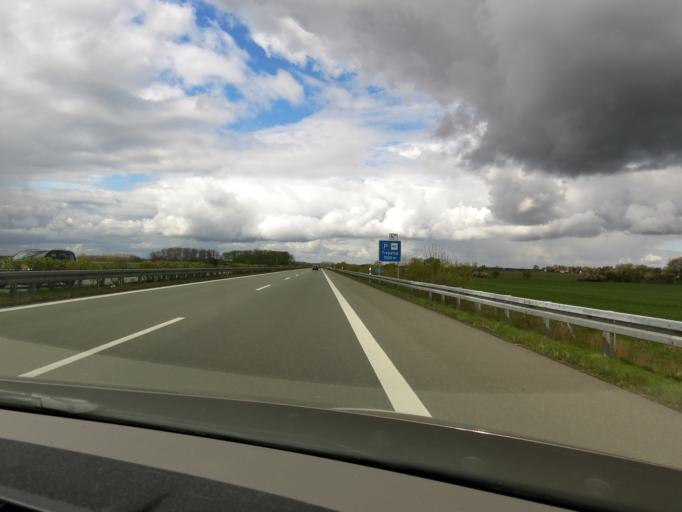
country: DE
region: Mecklenburg-Vorpommern
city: Franzburg
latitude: 54.0744
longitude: 12.8958
